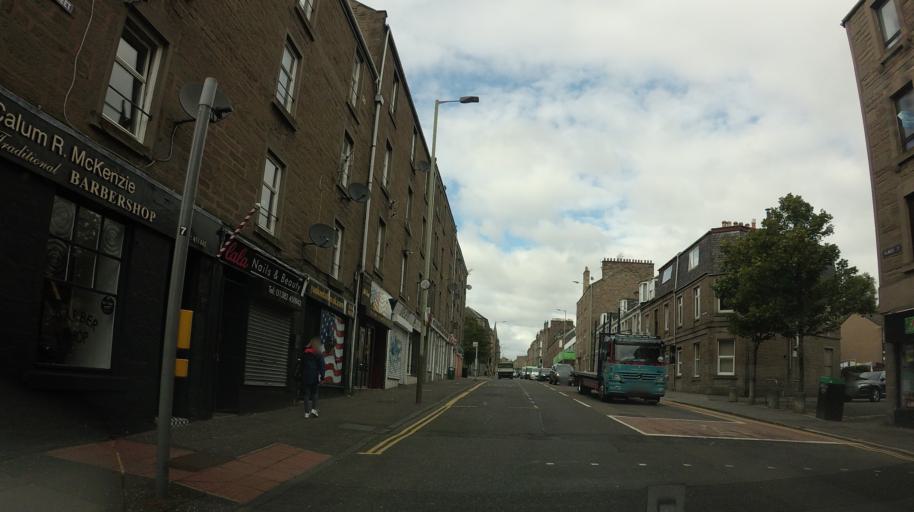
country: GB
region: Scotland
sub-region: Dundee City
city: Dundee
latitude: 56.4695
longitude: -2.9576
